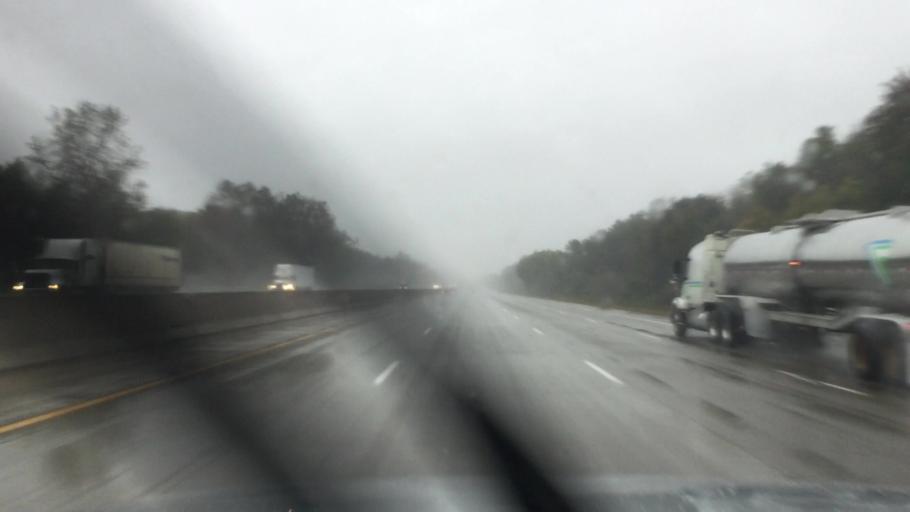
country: US
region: Michigan
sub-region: Saginaw County
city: Bridgeport
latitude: 43.3125
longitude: -83.8405
